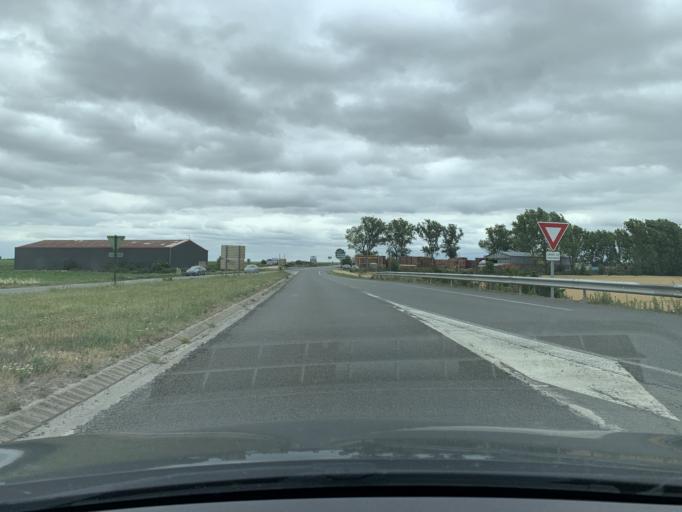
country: FR
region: Nord-Pas-de-Calais
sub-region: Departement du Pas-de-Calais
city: Marquion
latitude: 50.2056
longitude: 3.1072
